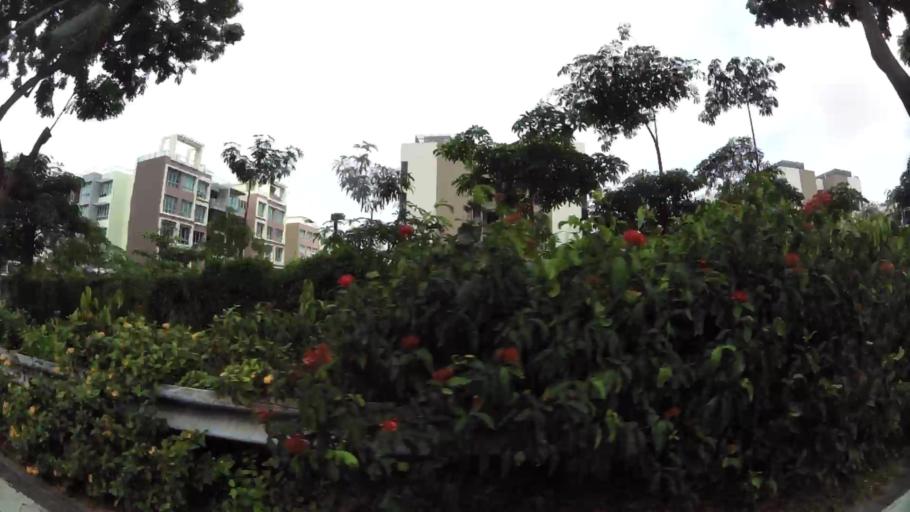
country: SG
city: Singapore
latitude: 1.3566
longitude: 103.9632
